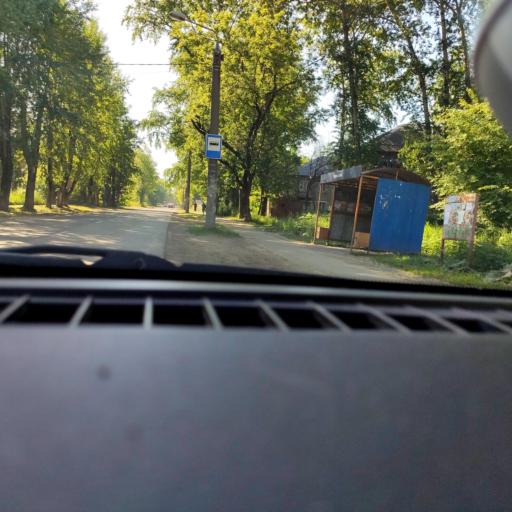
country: RU
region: Perm
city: Perm
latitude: 58.0932
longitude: 56.3784
